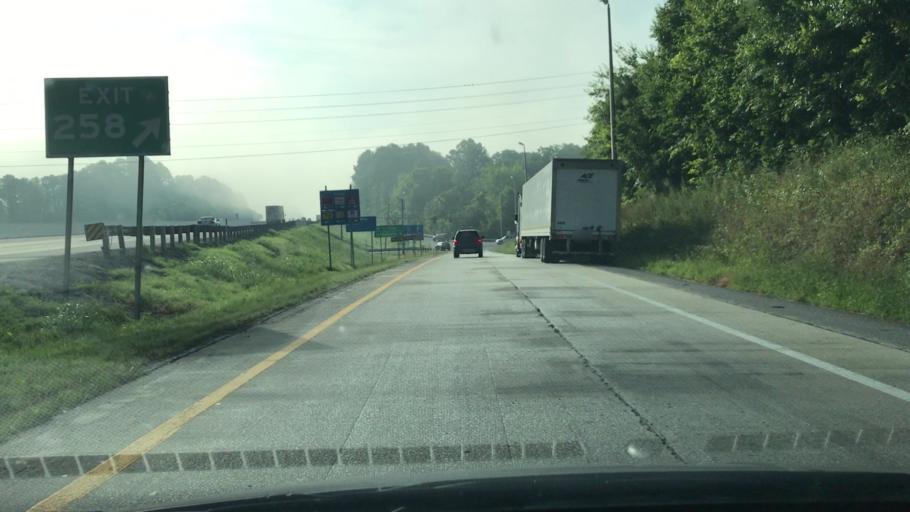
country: US
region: Tennessee
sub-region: Smith County
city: Gordonsville
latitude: 36.1791
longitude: -85.9495
